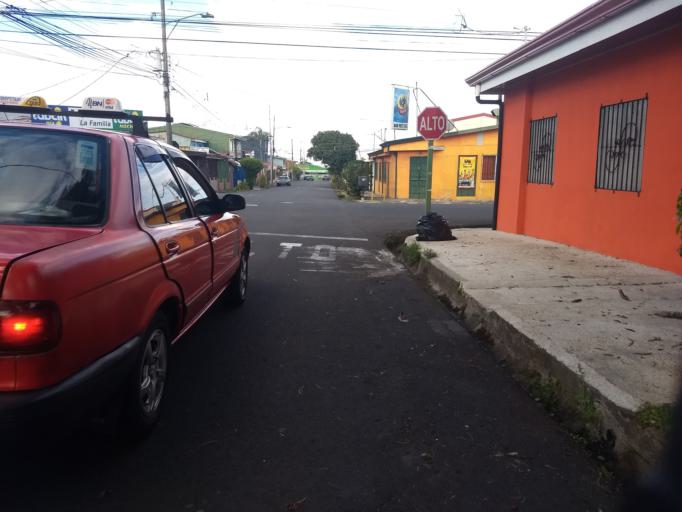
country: CR
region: San Jose
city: San Juan
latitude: 9.9582
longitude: -84.0835
